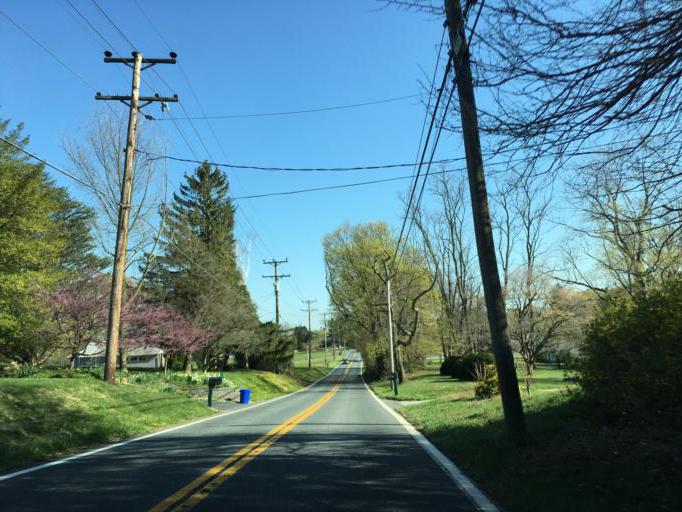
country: US
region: Maryland
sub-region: Baltimore County
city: Hampton
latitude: 39.4831
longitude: -76.5200
